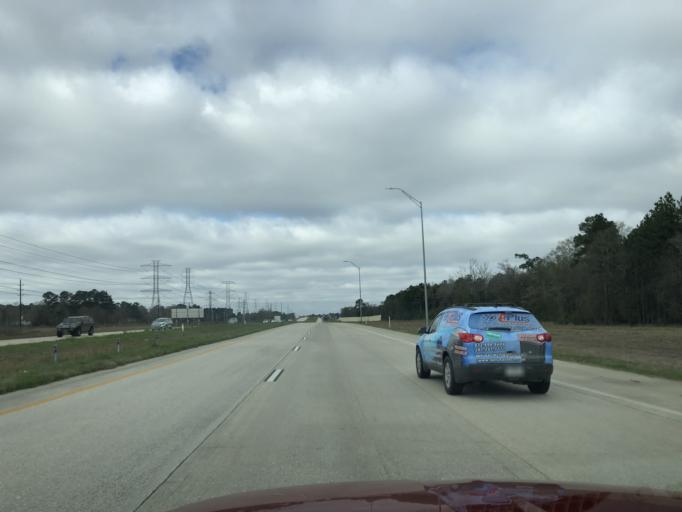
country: US
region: Texas
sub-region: Harris County
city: Spring
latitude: 30.0913
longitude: -95.4690
